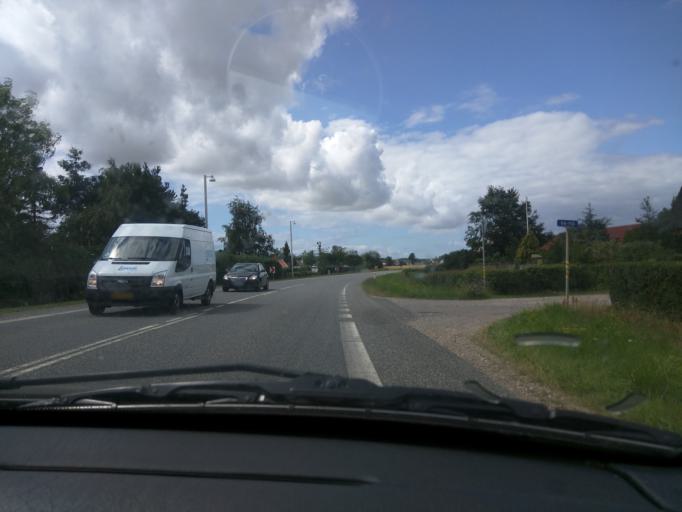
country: DK
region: Zealand
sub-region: Kalundborg Kommune
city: Svebolle
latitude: 55.6642
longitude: 11.2714
